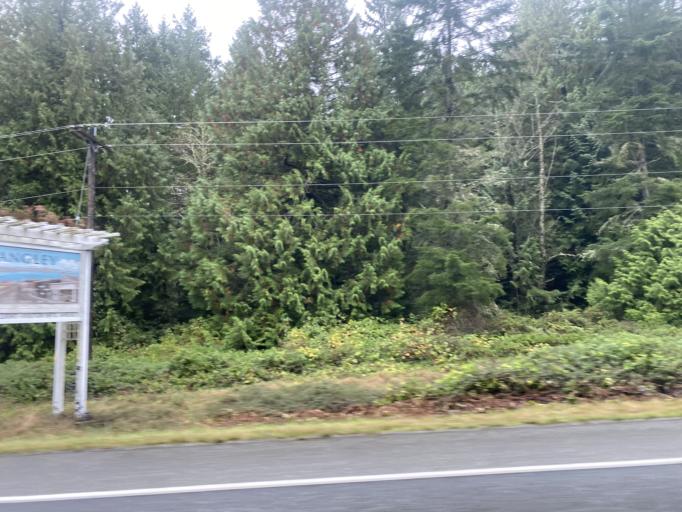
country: US
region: Washington
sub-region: Island County
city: Langley
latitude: 47.9862
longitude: -122.3918
